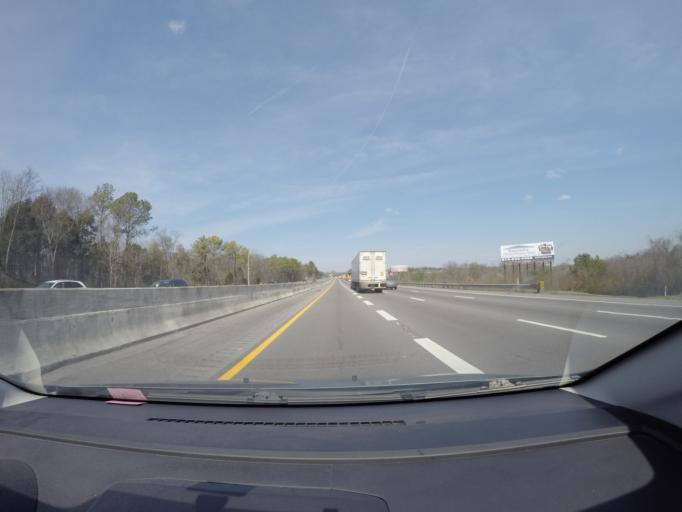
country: US
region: Tennessee
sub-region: Williamson County
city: Brentwood Estates
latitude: 36.0621
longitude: -86.6818
